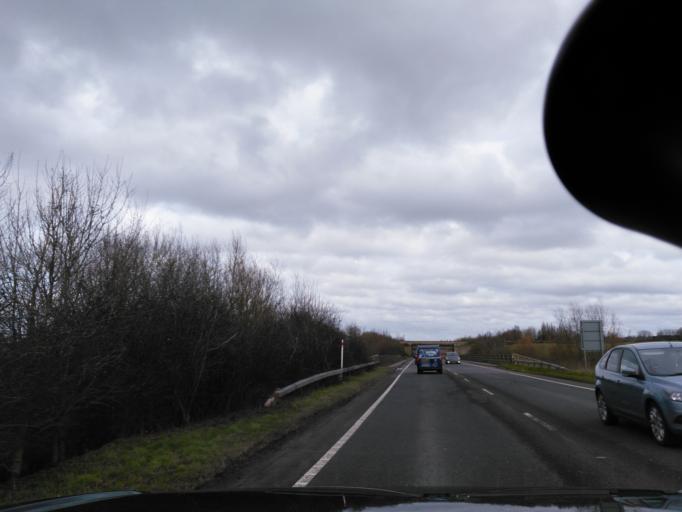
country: GB
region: England
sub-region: Wiltshire
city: Melksham
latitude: 51.3440
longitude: -2.1388
